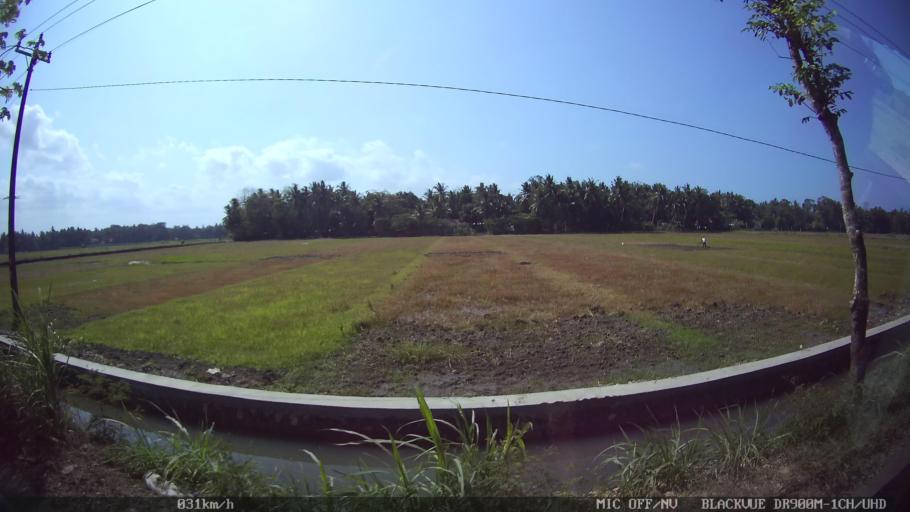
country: ID
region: Daerah Istimewa Yogyakarta
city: Srandakan
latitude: -7.9536
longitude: 110.2181
